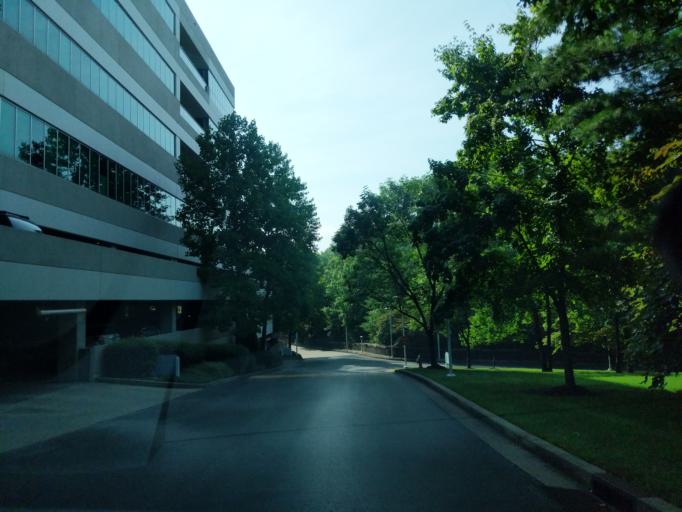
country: US
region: Tennessee
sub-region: Davidson County
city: Goodlettsville
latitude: 36.3090
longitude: -86.7000
